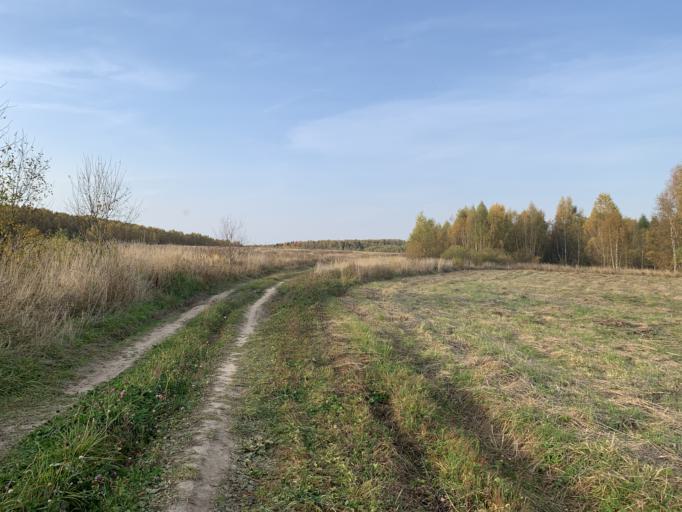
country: RU
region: Jaroslavl
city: Porech'ye-Rybnoye
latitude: 56.9817
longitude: 39.3844
